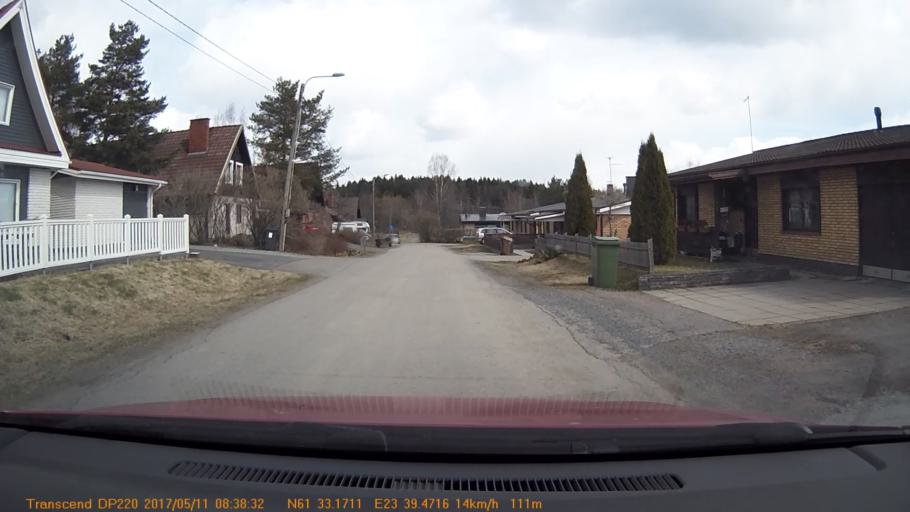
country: FI
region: Pirkanmaa
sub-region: Tampere
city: Yloejaervi
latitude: 61.5529
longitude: 23.6579
